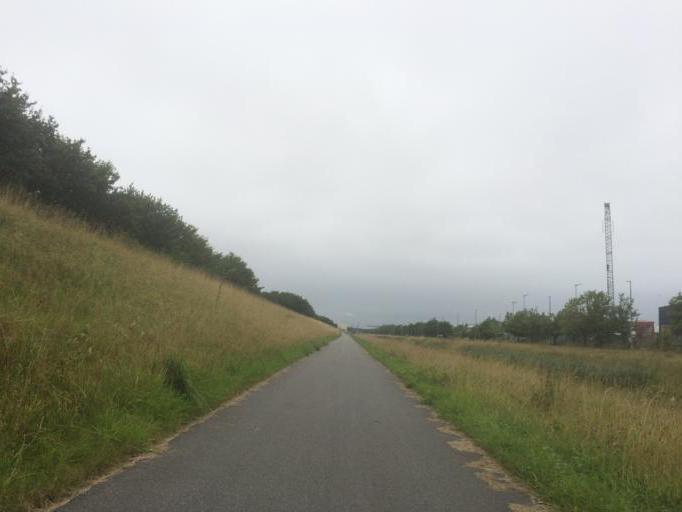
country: DK
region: Capital Region
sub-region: Hvidovre Kommune
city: Hvidovre
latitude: 55.6051
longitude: 12.4768
